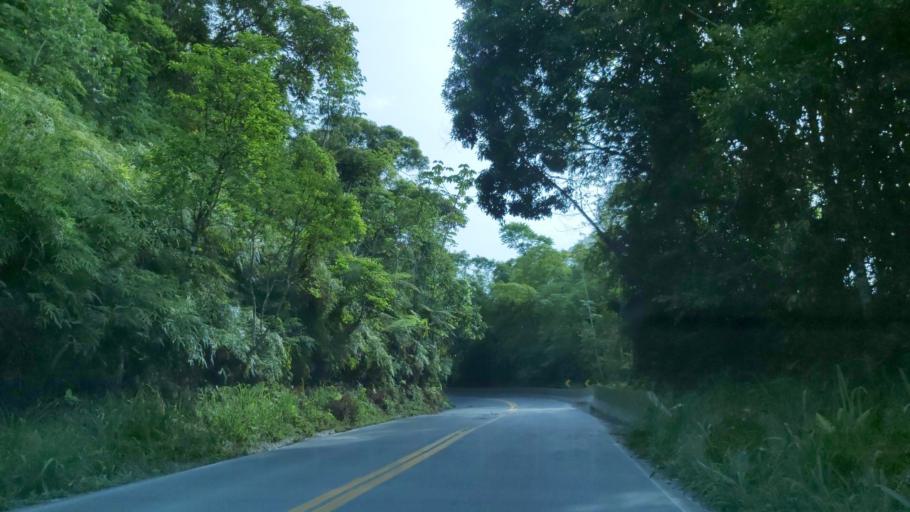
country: BR
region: Sao Paulo
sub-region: Juquia
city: Juquia
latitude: -24.1105
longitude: -47.6274
